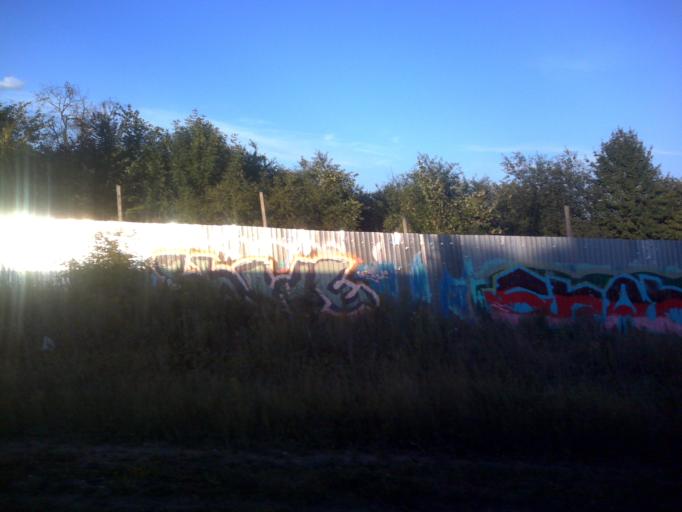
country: RU
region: Moscow
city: Tsaritsyno
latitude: 55.6228
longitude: 37.6304
